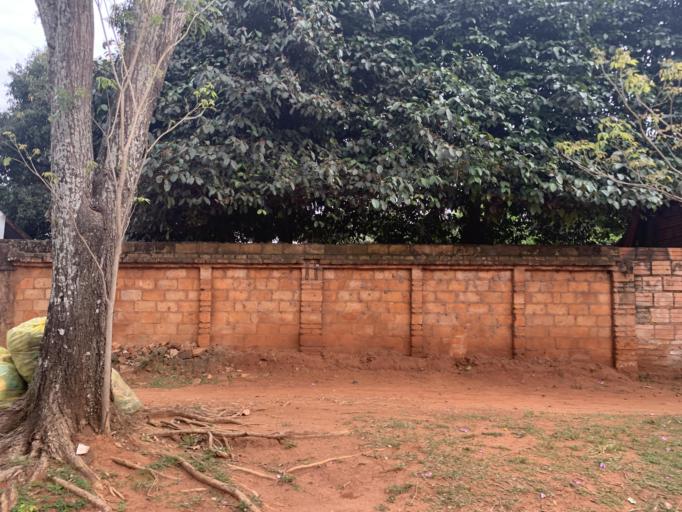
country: PY
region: Misiones
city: San Juan Bautista
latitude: -26.6674
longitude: -57.1519
